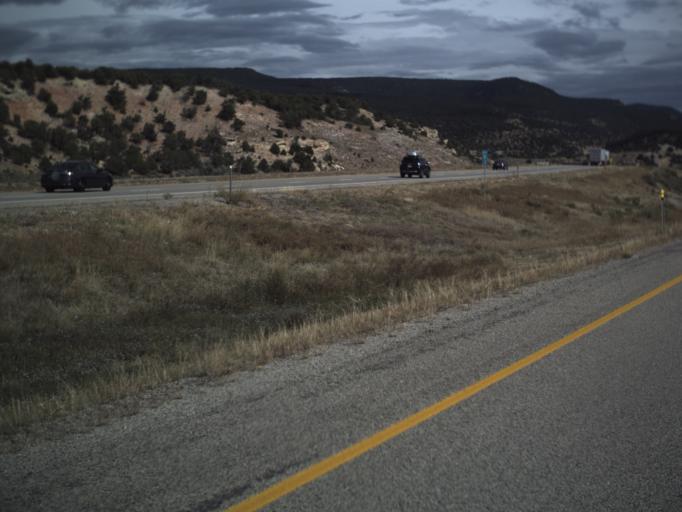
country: US
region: Utah
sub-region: Sevier County
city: Salina
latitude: 38.9169
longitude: -111.7448
